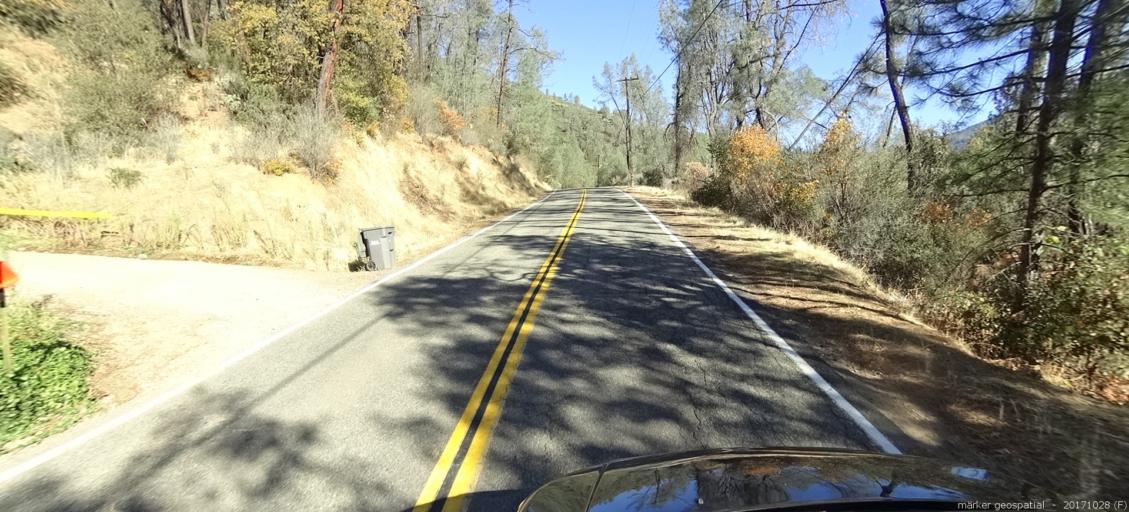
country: US
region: California
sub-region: Trinity County
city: Lewiston
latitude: 40.7427
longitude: -122.6256
